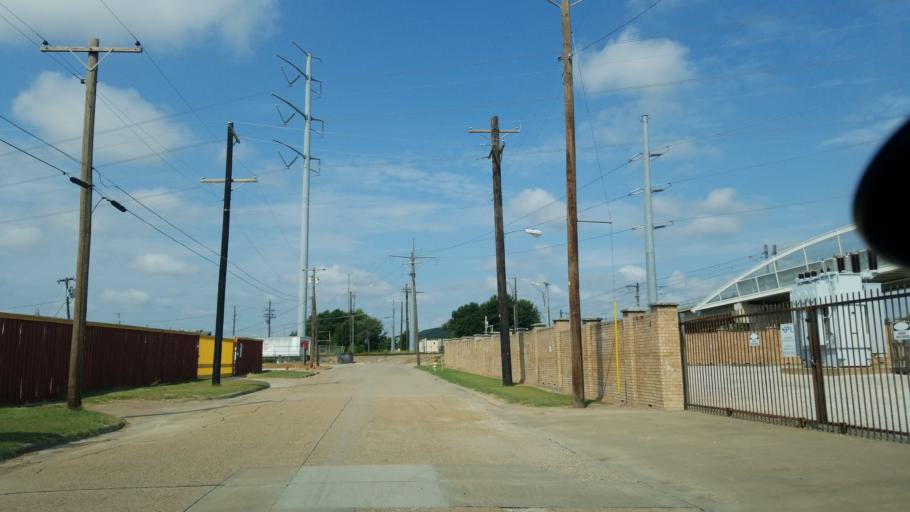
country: US
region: Texas
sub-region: Dallas County
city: Garland
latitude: 32.9162
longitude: -96.6318
